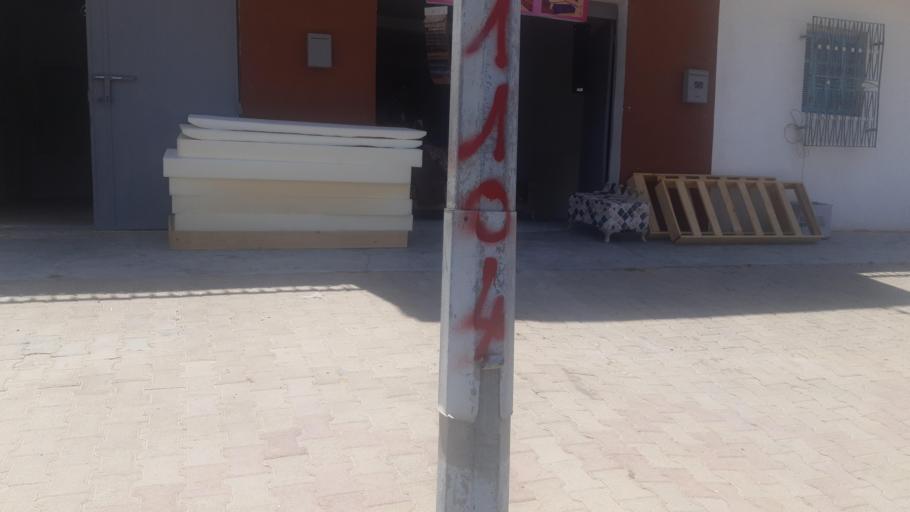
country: TN
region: Madanin
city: Bin Qirdan
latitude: 33.1385
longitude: 11.2020
